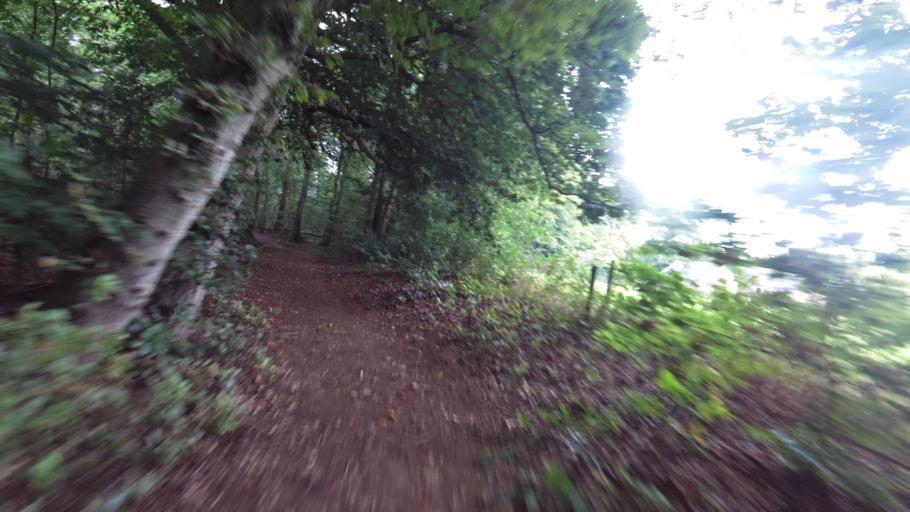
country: NL
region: Gelderland
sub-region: Gemeente Renkum
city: Renkum
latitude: 51.9890
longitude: 5.7286
